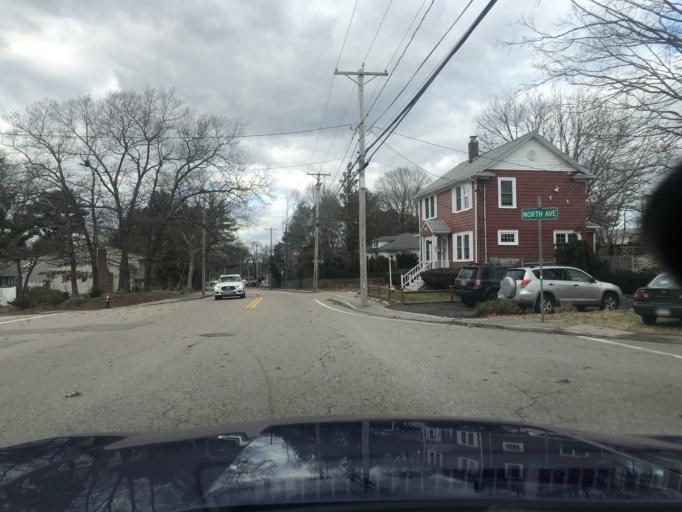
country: US
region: Massachusetts
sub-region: Plymouth County
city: Brockton
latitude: 42.1079
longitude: -71.0068
